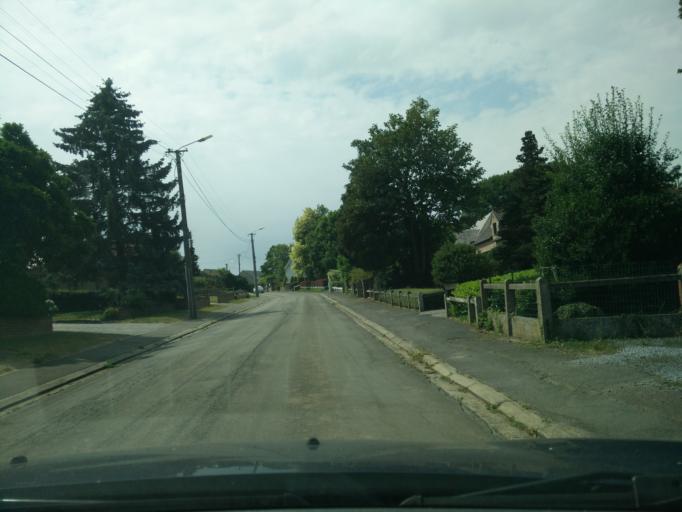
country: BE
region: Wallonia
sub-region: Province du Hainaut
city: Braine-le-Comte
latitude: 50.6451
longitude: 4.1759
